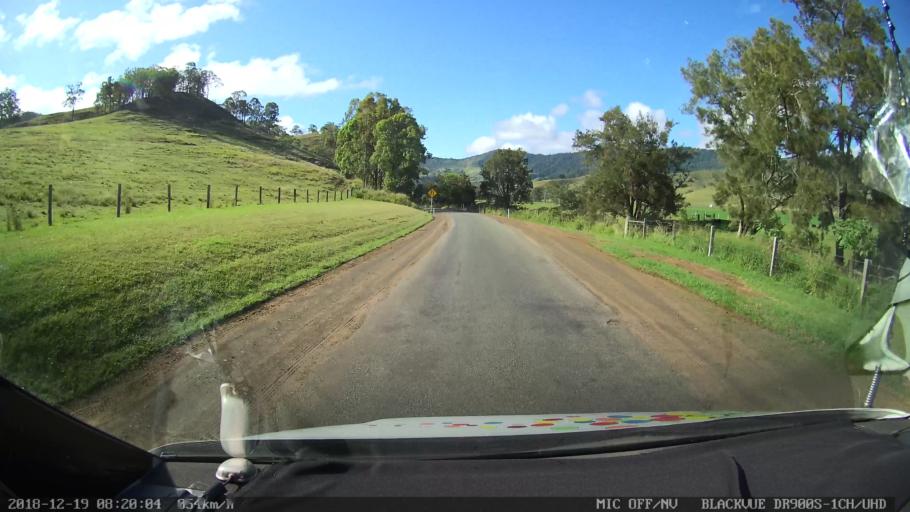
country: AU
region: New South Wales
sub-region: Kyogle
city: Kyogle
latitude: -28.2873
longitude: 152.9099
